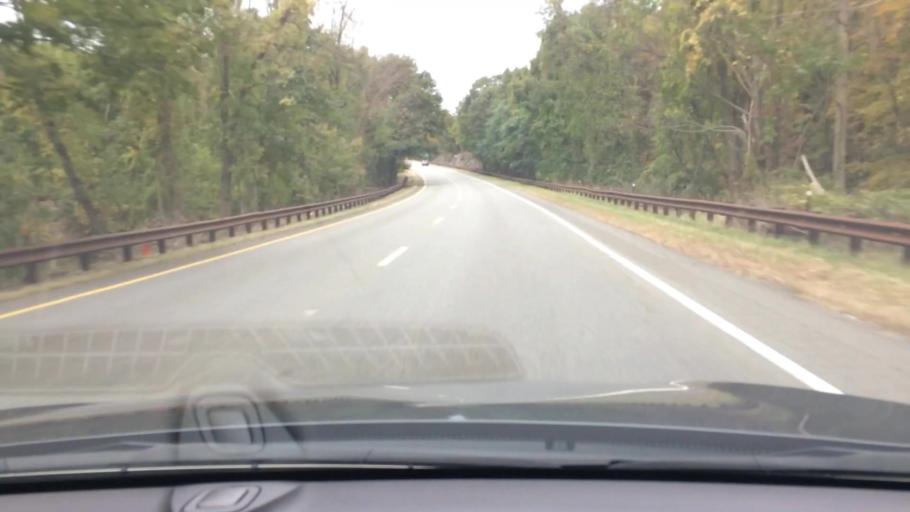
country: US
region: New York
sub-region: Westchester County
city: Hastings-on-Hudson
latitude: 40.9880
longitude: -73.9119
